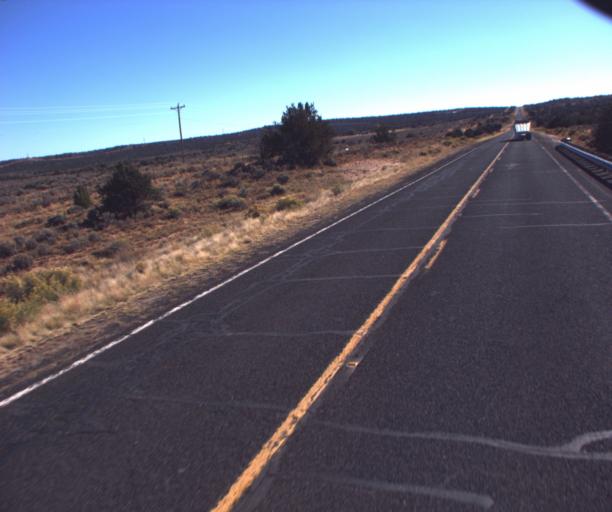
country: US
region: Arizona
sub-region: Apache County
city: Ganado
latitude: 35.6985
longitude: -109.5449
